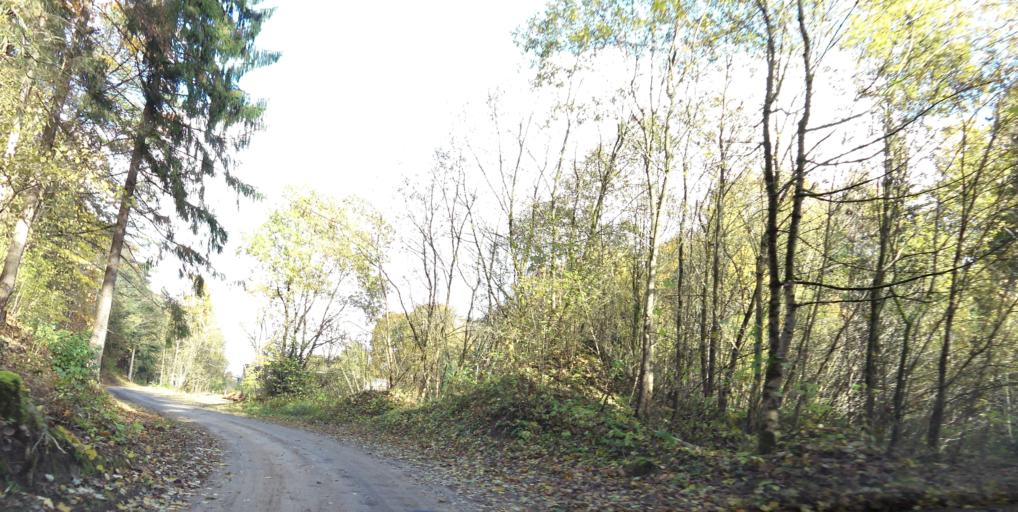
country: LT
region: Vilnius County
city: Vilkpede
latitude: 54.6552
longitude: 25.2575
